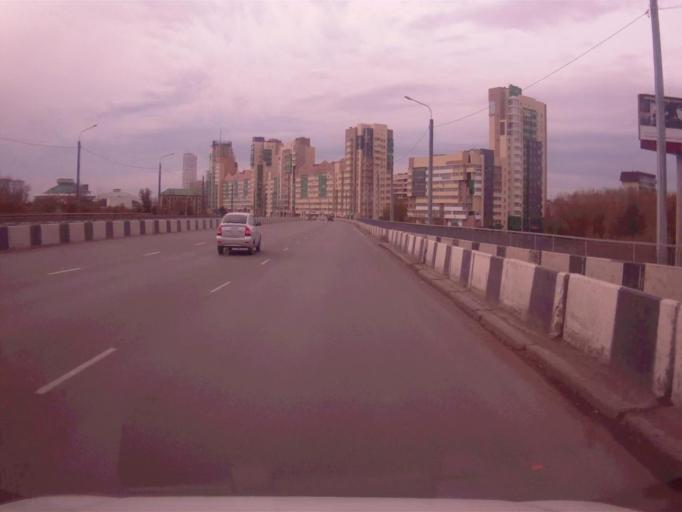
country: RU
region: Chelyabinsk
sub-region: Gorod Chelyabinsk
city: Chelyabinsk
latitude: 55.1728
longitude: 61.4099
